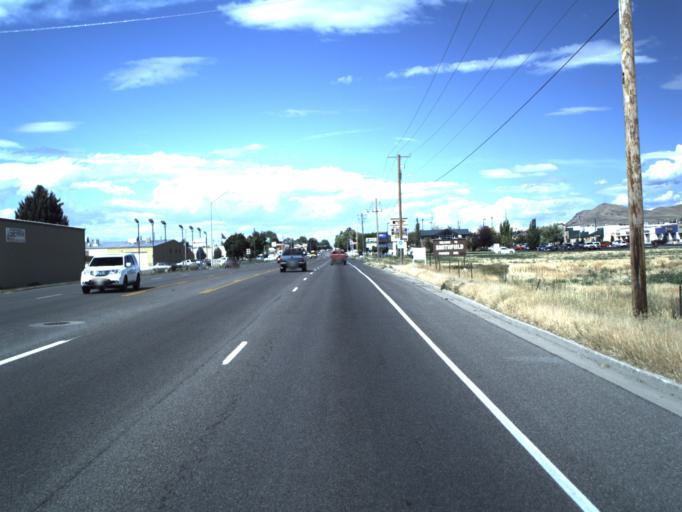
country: US
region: Utah
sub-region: Cache County
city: Hyde Park
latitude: 41.8154
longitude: -111.8331
